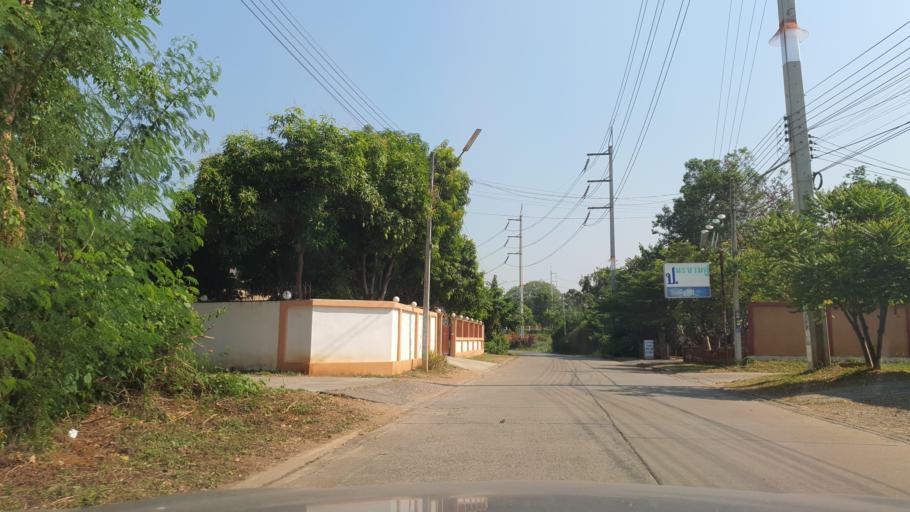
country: TH
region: Kanchanaburi
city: Kanchanaburi
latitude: 14.0671
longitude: 99.4859
